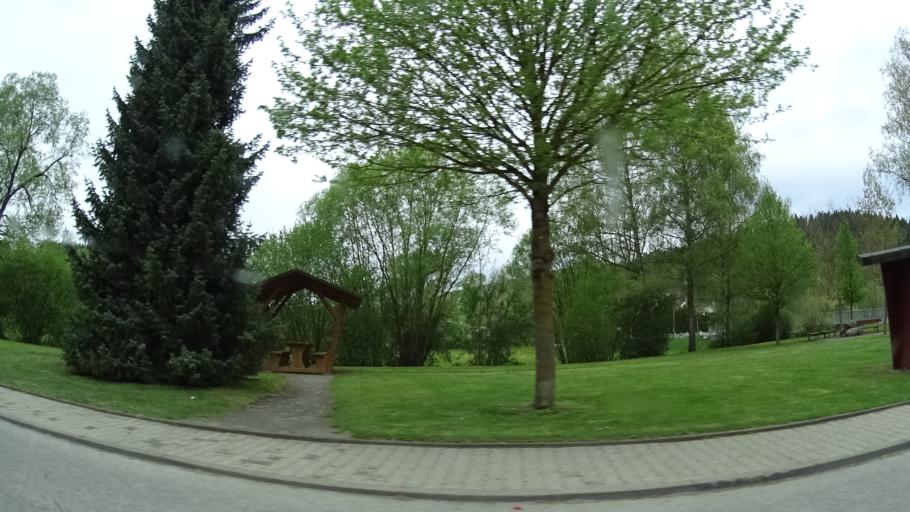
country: DE
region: Baden-Wuerttemberg
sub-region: Freiburg Region
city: Niedereschach
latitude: 48.1470
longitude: 8.5497
